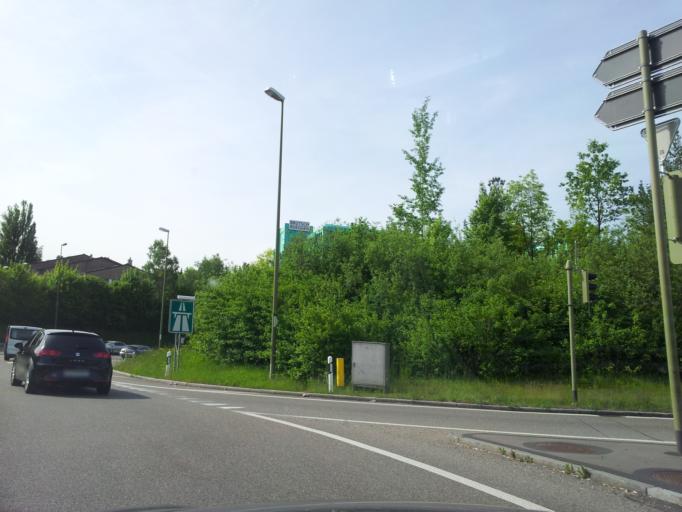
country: CH
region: Zurich
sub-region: Bezirk Dietikon
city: Dietikon / Hofacker
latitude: 47.3949
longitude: 8.4190
